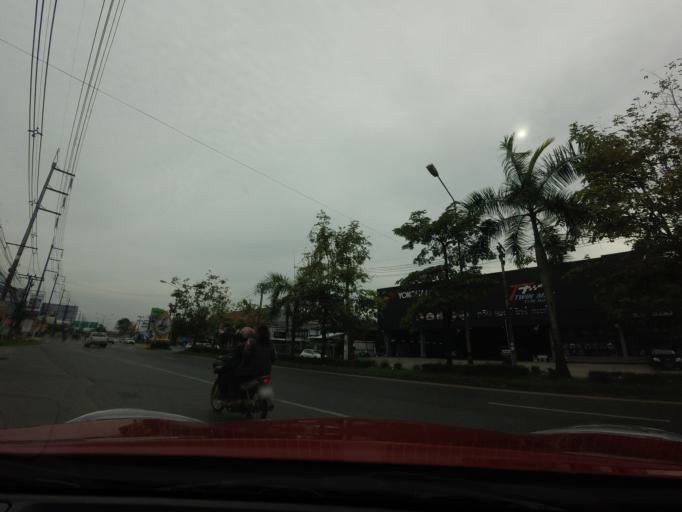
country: TH
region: Songkhla
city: Hat Yai
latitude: 6.9798
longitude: 100.4807
